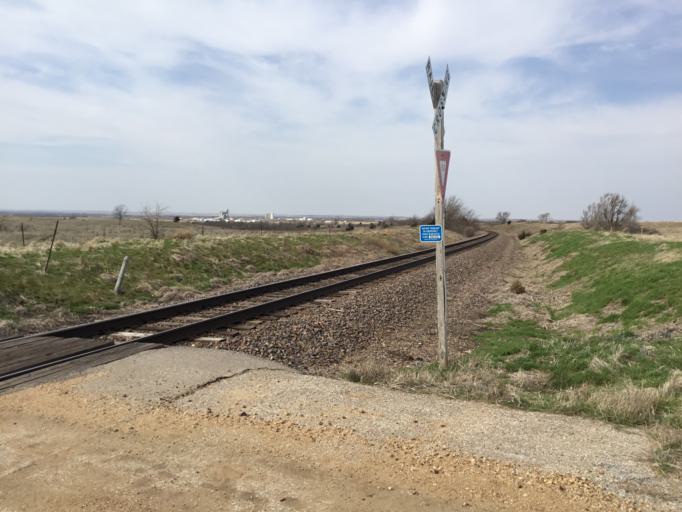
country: US
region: Kansas
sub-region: Ellsworth County
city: Ellsworth
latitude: 38.7324
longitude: -98.1140
